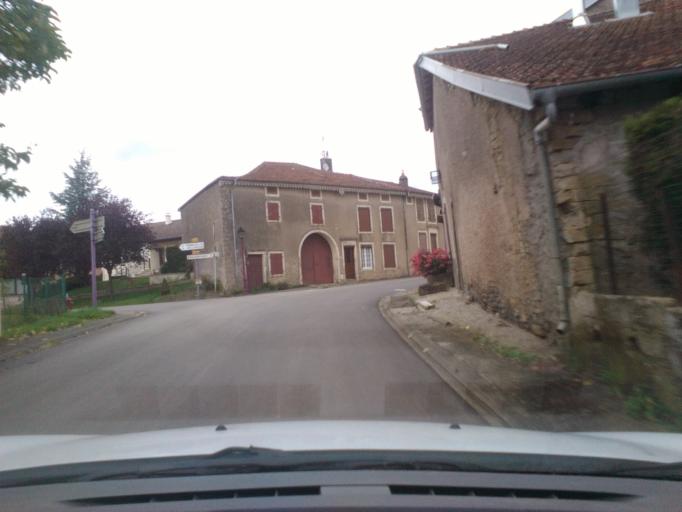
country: FR
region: Lorraine
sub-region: Departement des Vosges
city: Mirecourt
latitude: 48.3557
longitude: 6.0855
